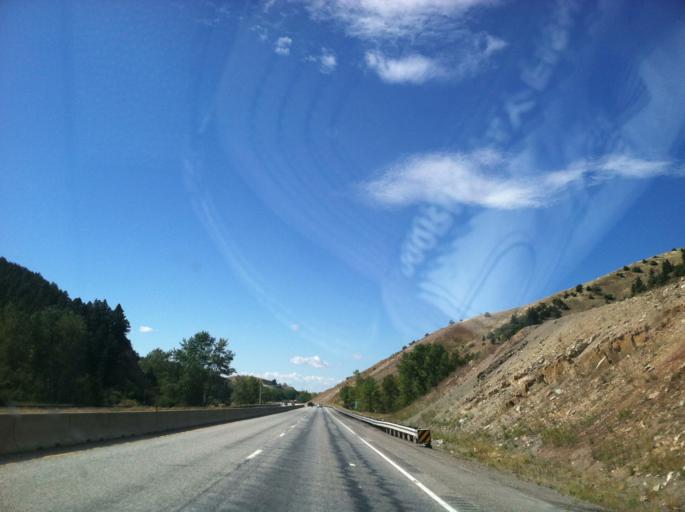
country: US
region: Montana
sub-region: Gallatin County
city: Bozeman
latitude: 45.6412
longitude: -110.9196
